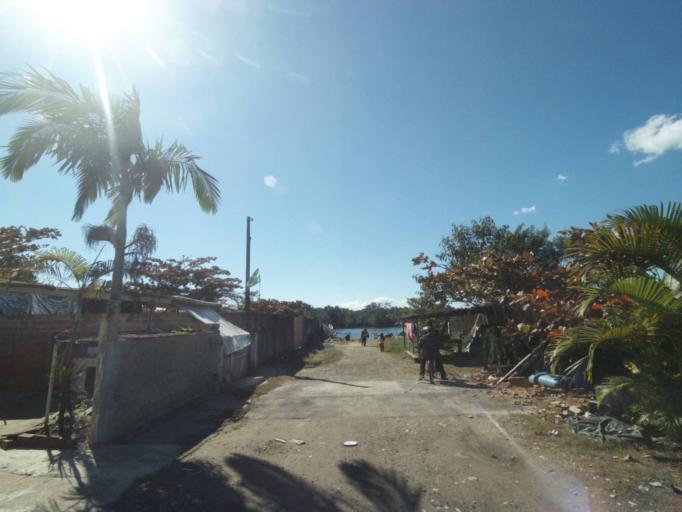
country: BR
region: Parana
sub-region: Paranagua
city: Paranagua
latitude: -25.5122
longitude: -48.4990
